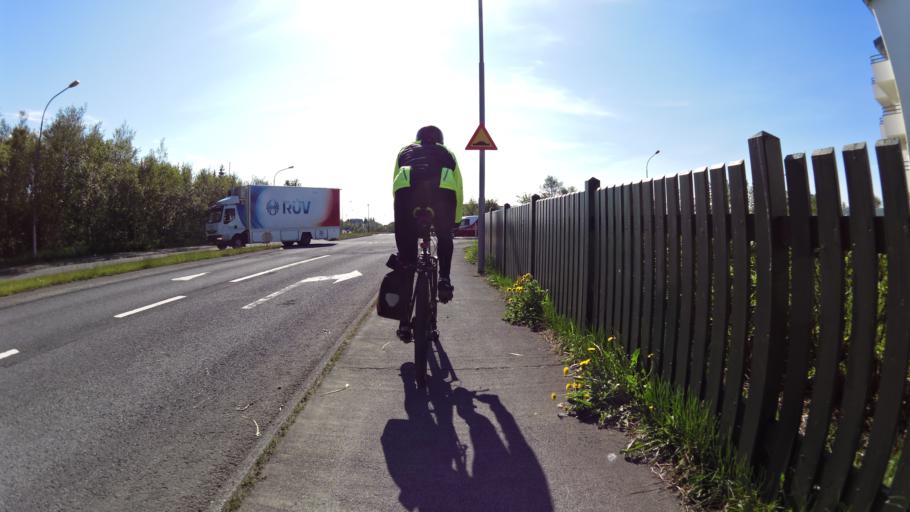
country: IS
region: Capital Region
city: Reykjavik
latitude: 64.1276
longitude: -21.8927
